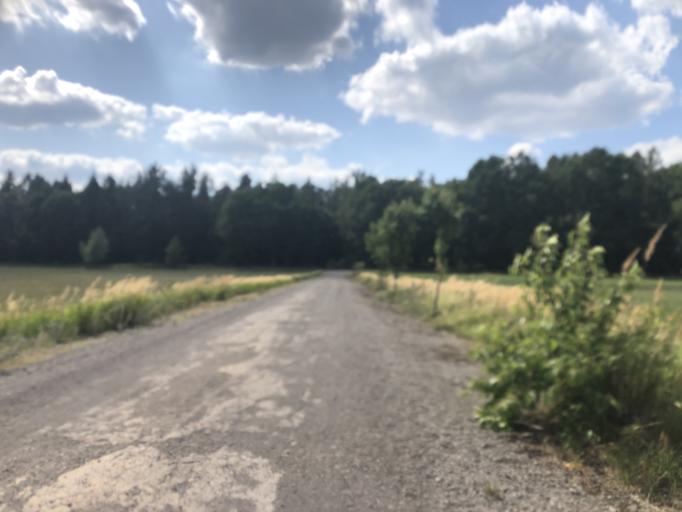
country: DE
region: Brandenburg
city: Mullrose
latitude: 52.2307
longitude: 14.3939
